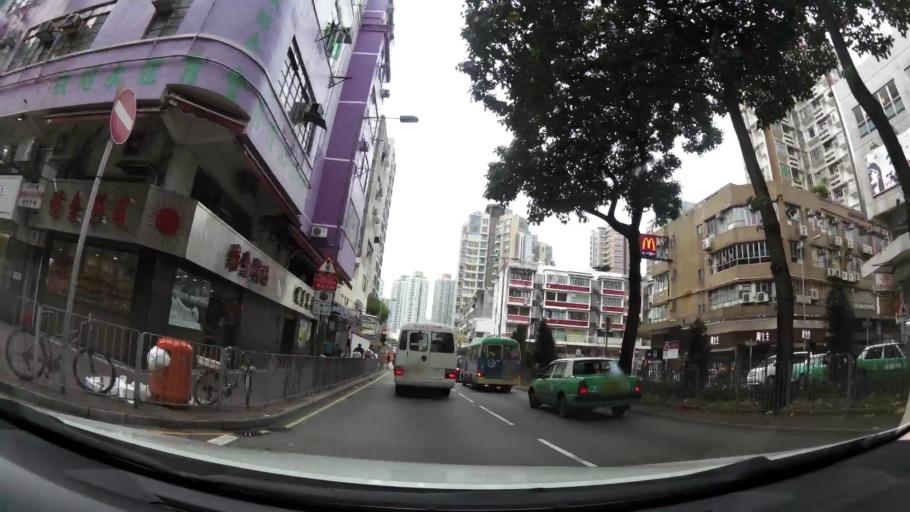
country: HK
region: Tai Po
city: Tai Po
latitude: 22.4483
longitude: 114.1665
